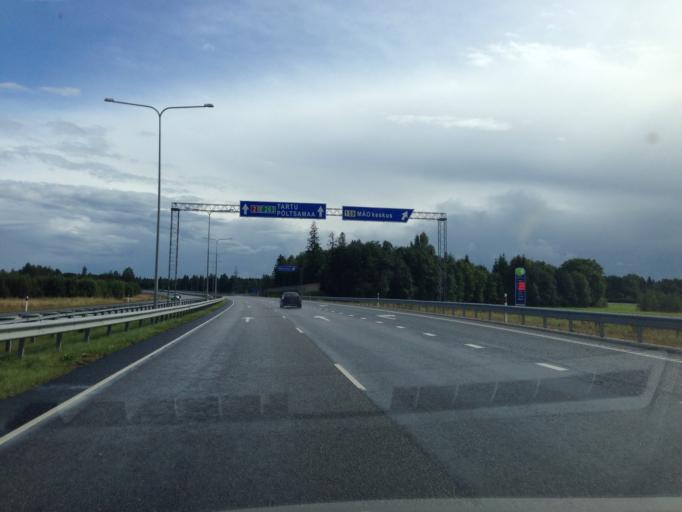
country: EE
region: Jaervamaa
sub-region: Paide linn
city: Paide
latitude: 58.9050
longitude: 25.6324
